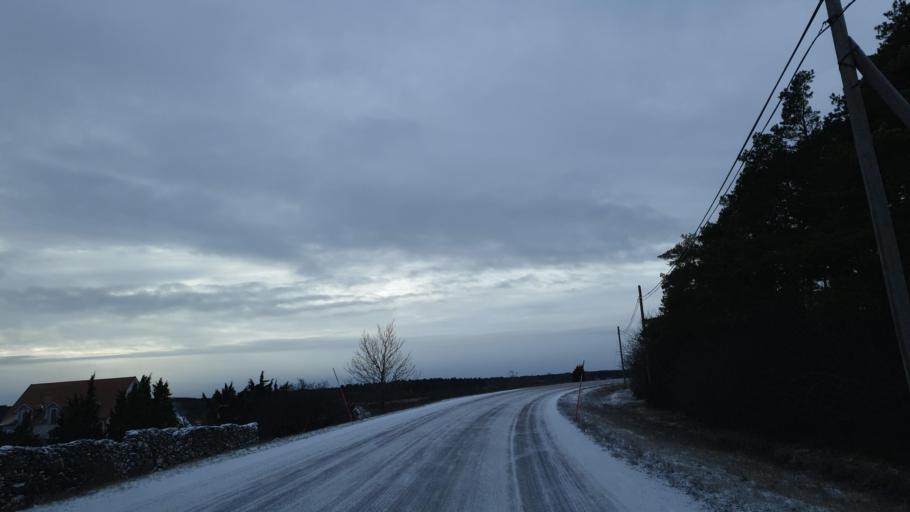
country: SE
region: Gotland
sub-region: Gotland
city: Slite
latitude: 57.4212
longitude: 18.8961
